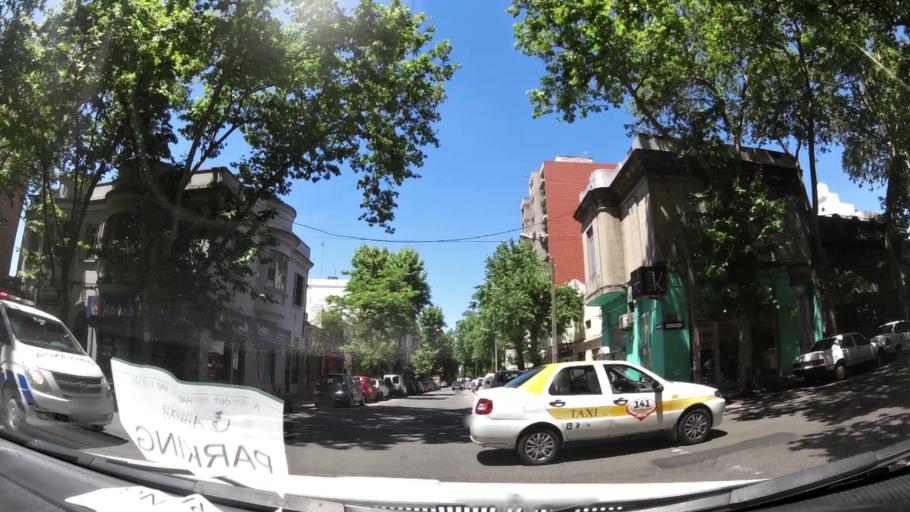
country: UY
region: Montevideo
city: Montevideo
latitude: -34.9020
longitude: -56.1679
